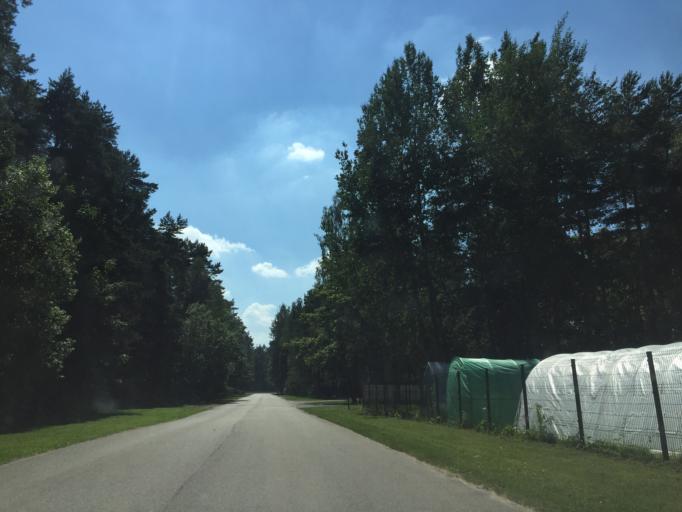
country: LV
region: Babite
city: Pinki
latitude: 56.9521
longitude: 23.9508
